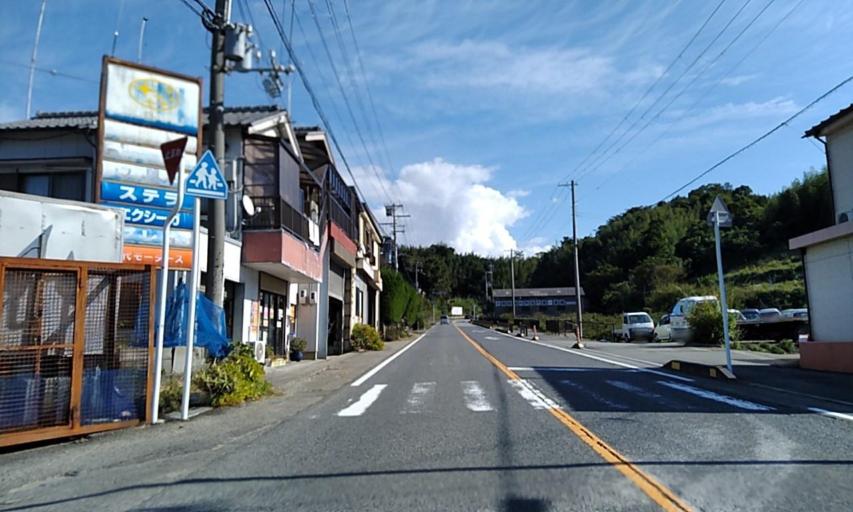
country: JP
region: Wakayama
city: Tanabe
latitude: 33.7820
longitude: 135.2882
